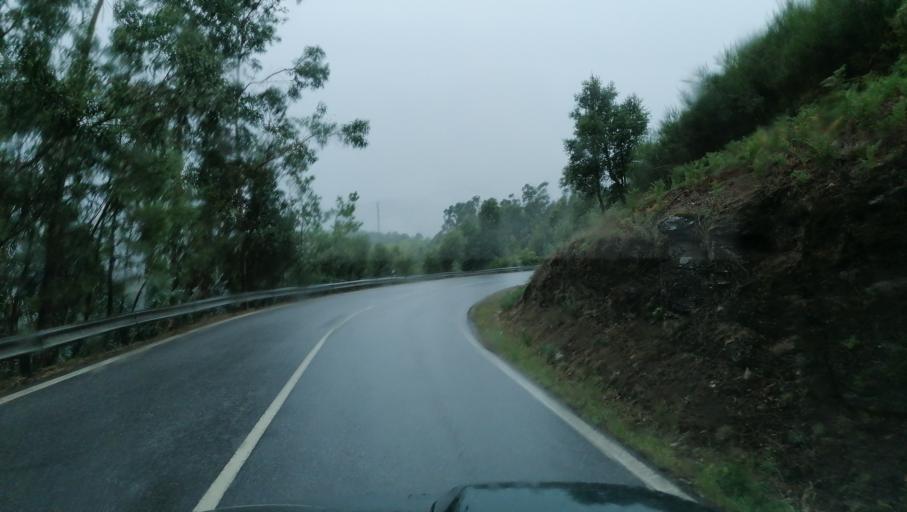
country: PT
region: Braga
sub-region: Cabeceiras de Basto
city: Cabeceiras de Basto
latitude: 41.4898
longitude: -7.9353
